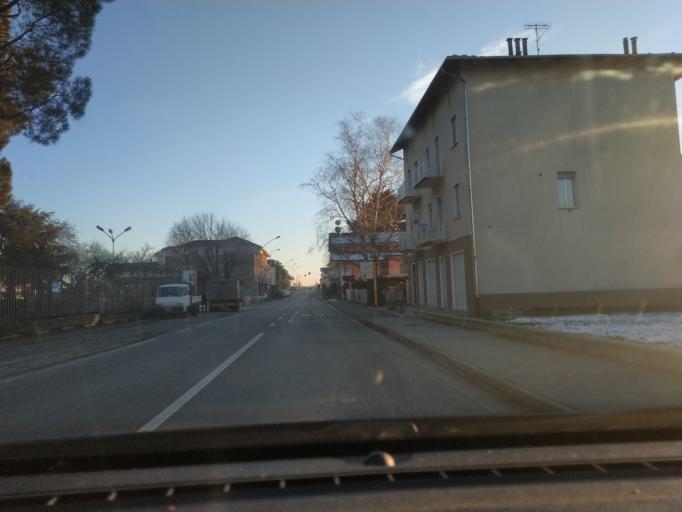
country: IT
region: Piedmont
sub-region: Provincia di Torino
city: Romano Canavese
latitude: 45.4273
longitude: 7.8825
